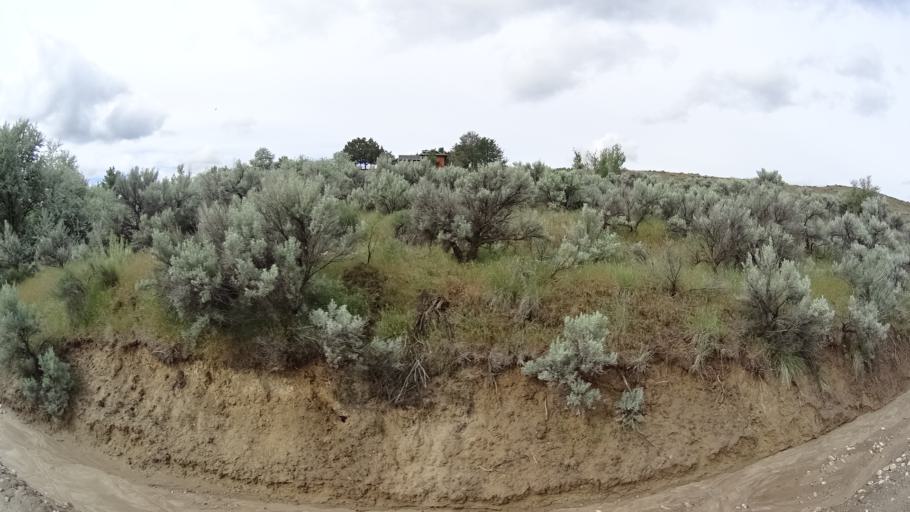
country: US
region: Idaho
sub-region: Ada County
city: Eagle
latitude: 43.7508
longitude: -116.3596
